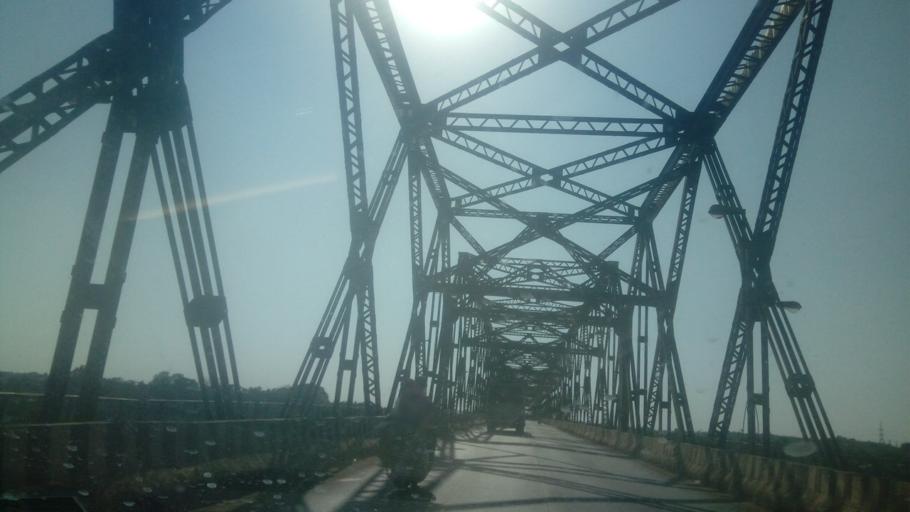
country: IN
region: Goa
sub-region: North Goa
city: Navelim
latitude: 15.5285
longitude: 73.9710
